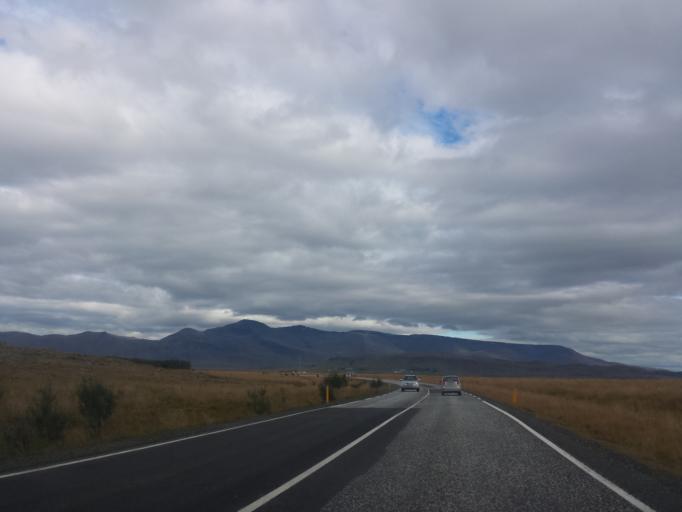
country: IS
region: Capital Region
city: Mosfellsbaer
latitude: 64.3525
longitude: -21.8083
